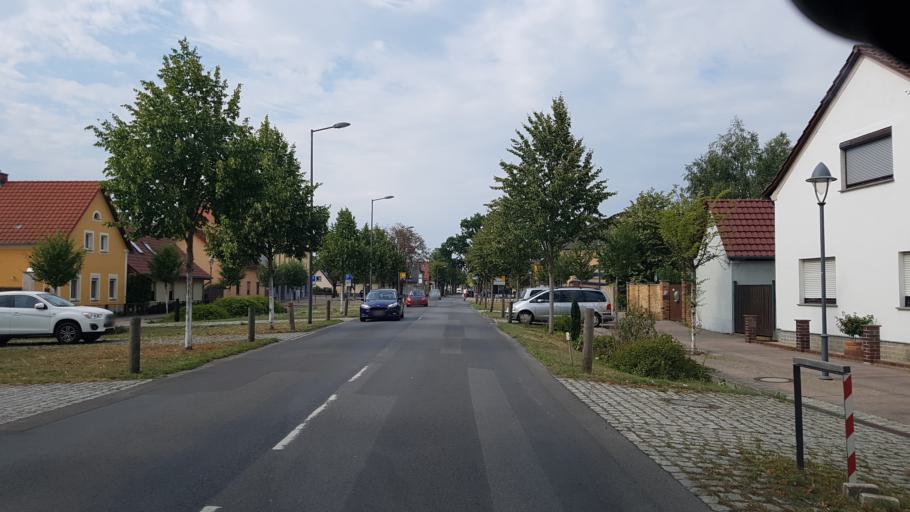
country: DE
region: Brandenburg
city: Lauchhammer
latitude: 51.4698
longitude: 13.7392
